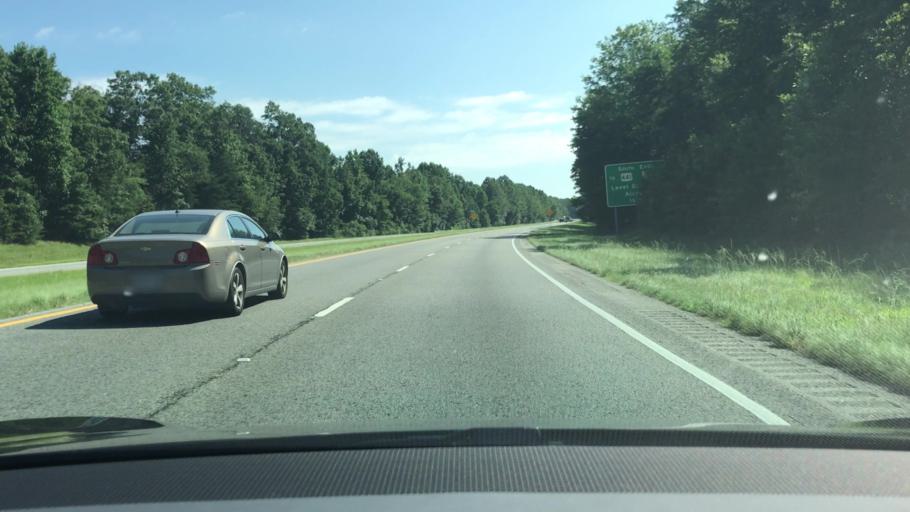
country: US
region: Georgia
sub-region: Habersham County
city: Baldwin
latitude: 34.5078
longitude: -83.5662
